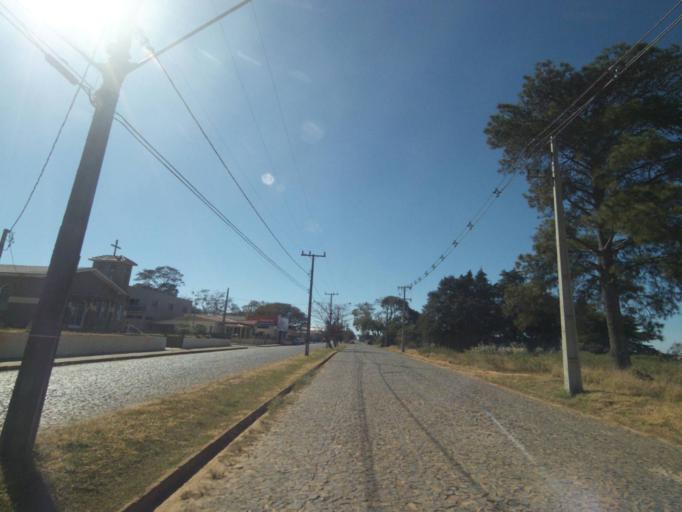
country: BR
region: Parana
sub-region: Reserva
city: Reserva
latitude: -24.6254
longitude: -50.6424
